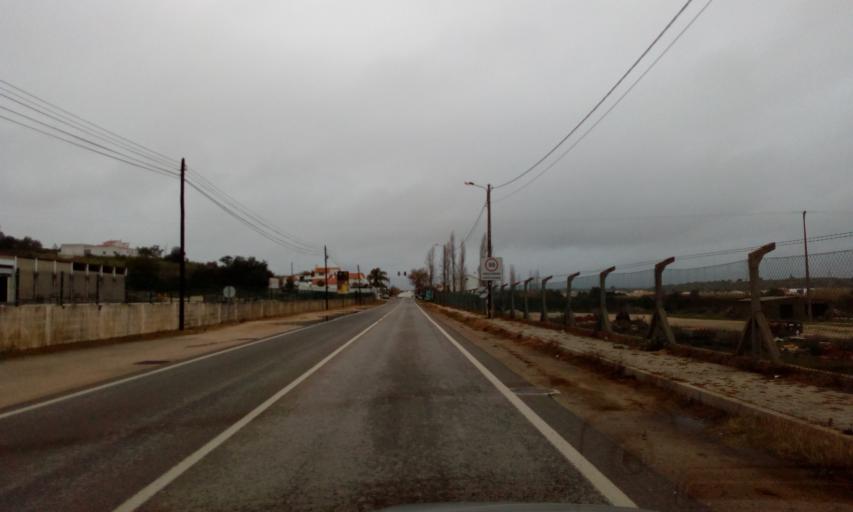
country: PT
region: Faro
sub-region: Albufeira
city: Guia
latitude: 37.1595
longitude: -8.2950
